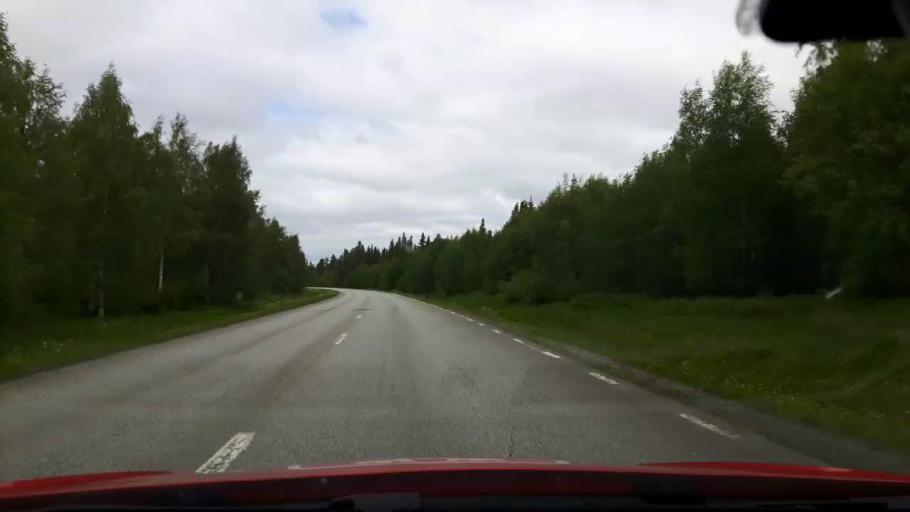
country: SE
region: Jaemtland
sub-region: Krokoms Kommun
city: Krokom
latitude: 63.4303
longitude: 14.4987
